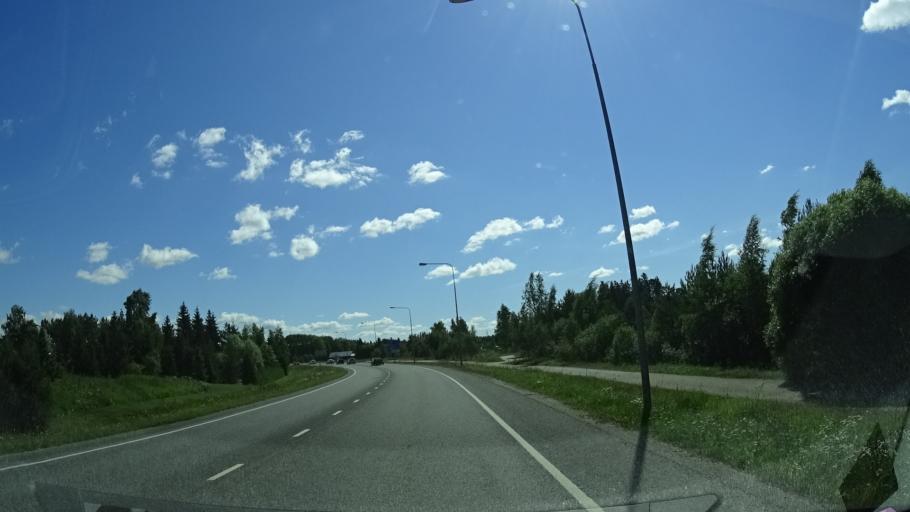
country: FI
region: Varsinais-Suomi
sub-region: Turku
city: Raisio
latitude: 60.5043
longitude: 22.1437
